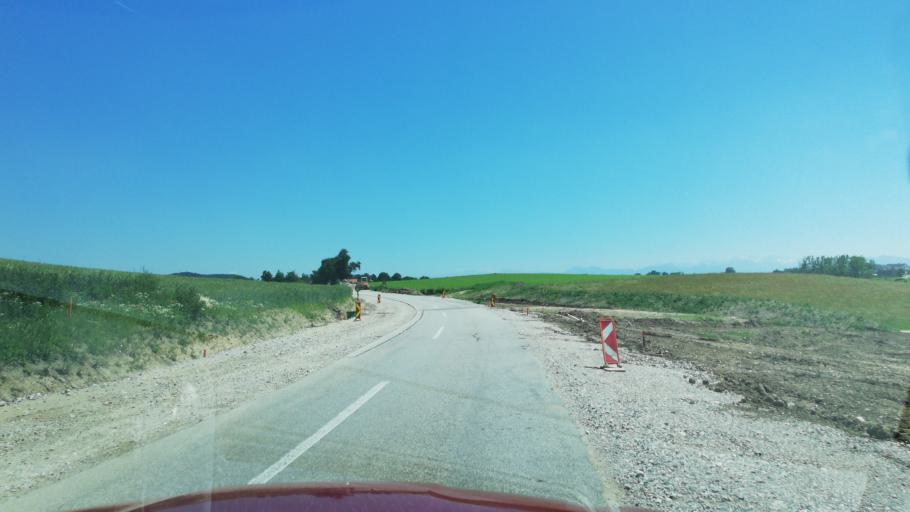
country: AT
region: Upper Austria
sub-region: Wels-Land
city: Bachmanning
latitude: 48.1304
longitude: 13.7707
